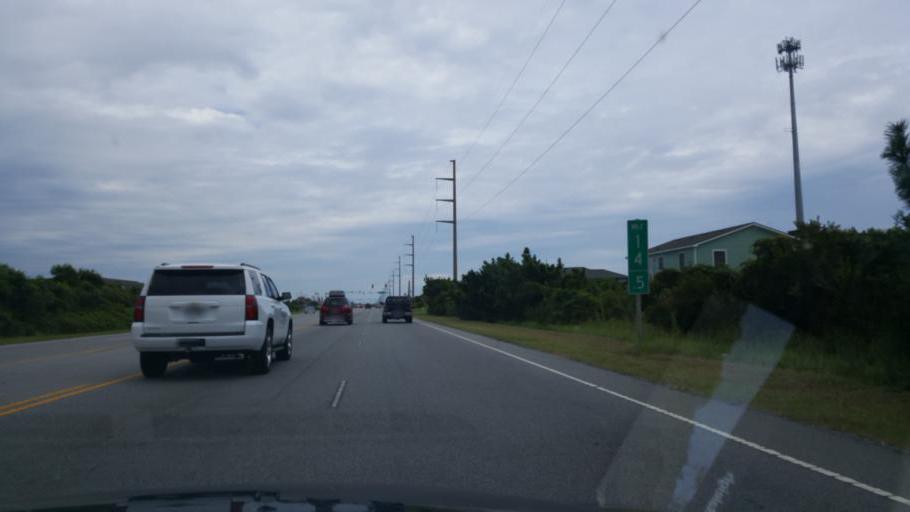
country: US
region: North Carolina
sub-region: Dare County
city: Nags Head
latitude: 35.9327
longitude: -75.6122
